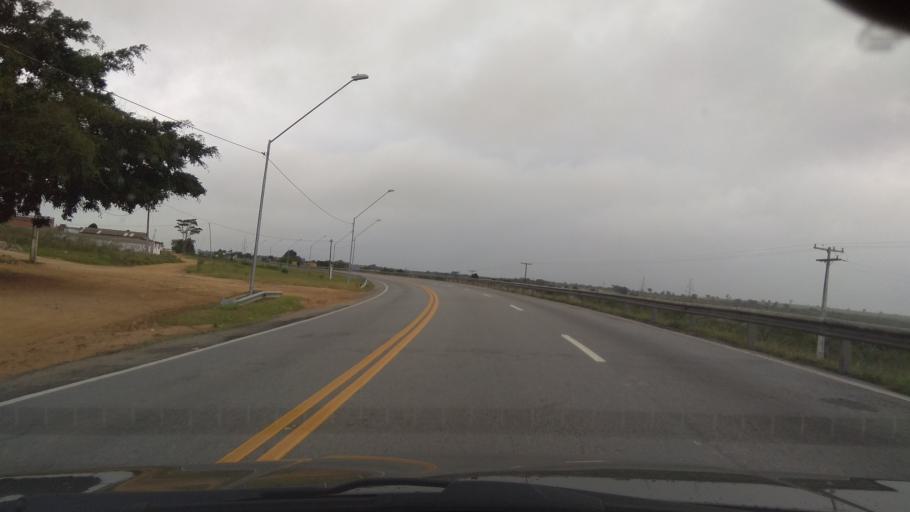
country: BR
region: Bahia
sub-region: Santa Ines
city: Santa Ines
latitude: -13.0666
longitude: -39.9602
